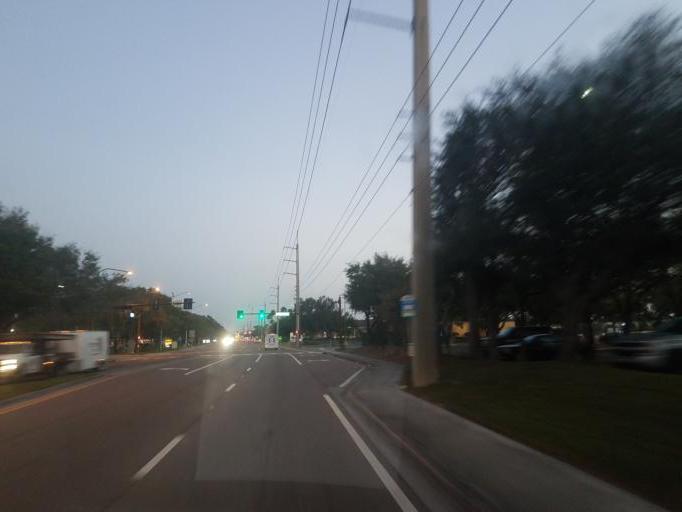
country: US
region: Florida
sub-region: Sarasota County
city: Lake Sarasota
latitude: 27.2942
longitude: -82.4517
